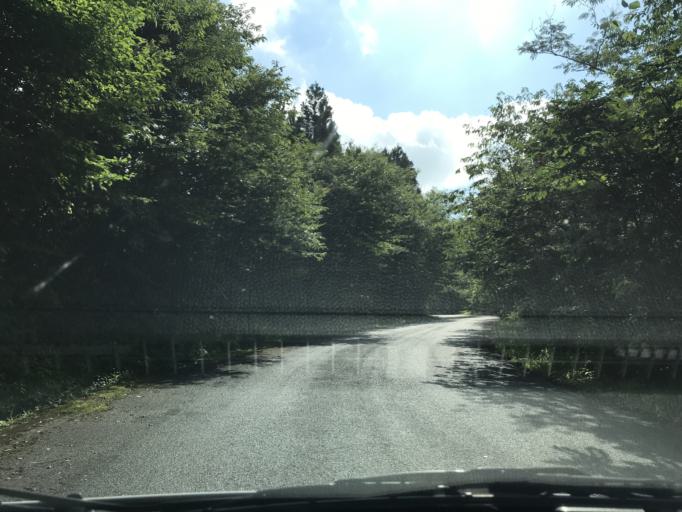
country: JP
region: Iwate
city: Mizusawa
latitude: 39.0277
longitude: 141.1988
